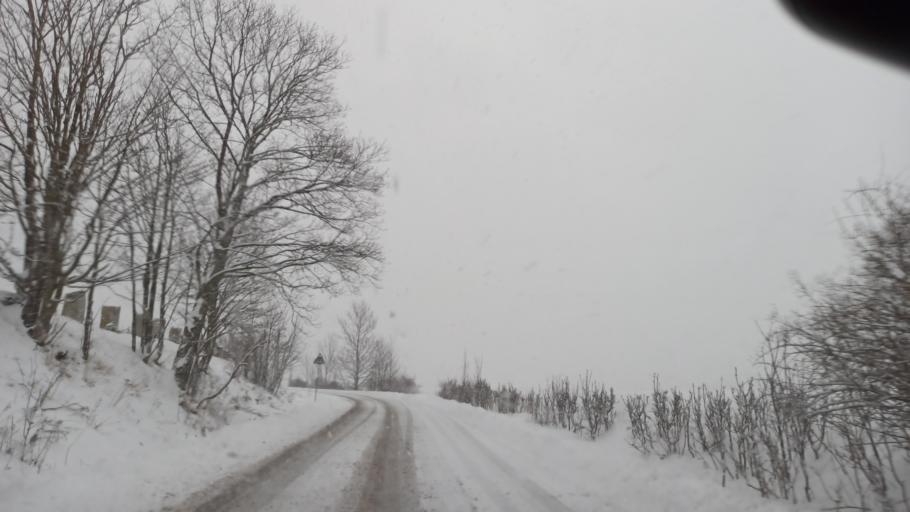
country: PL
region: Lower Silesian Voivodeship
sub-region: Powiat klodzki
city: Ludwikowice Klodzkie
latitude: 50.6462
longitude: 16.4841
